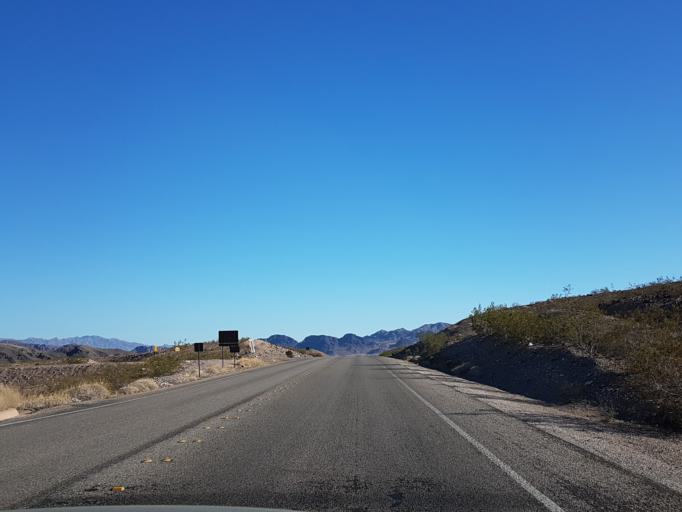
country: US
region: Nevada
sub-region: Clark County
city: Boulder City
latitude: 36.0786
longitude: -114.8235
